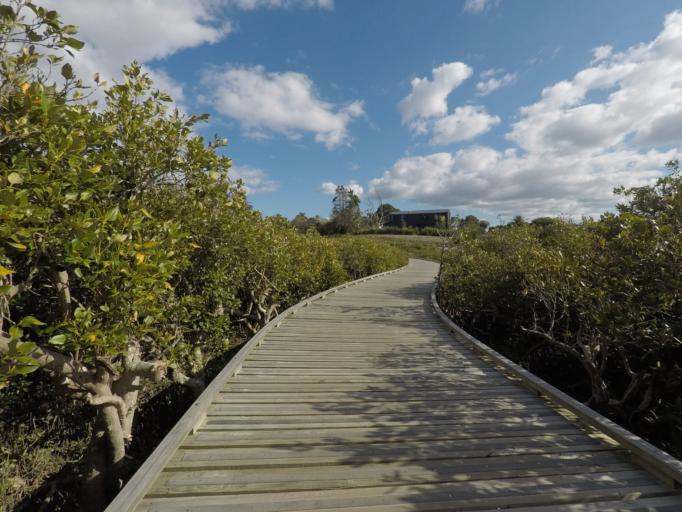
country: NZ
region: Auckland
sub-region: Auckland
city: Rosebank
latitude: -36.8861
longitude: 174.6941
